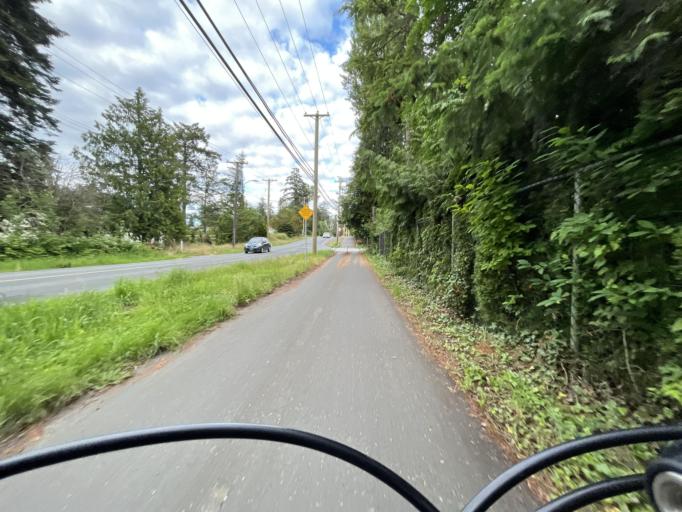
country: CA
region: British Columbia
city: Victoria
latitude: 48.4775
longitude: -123.3478
